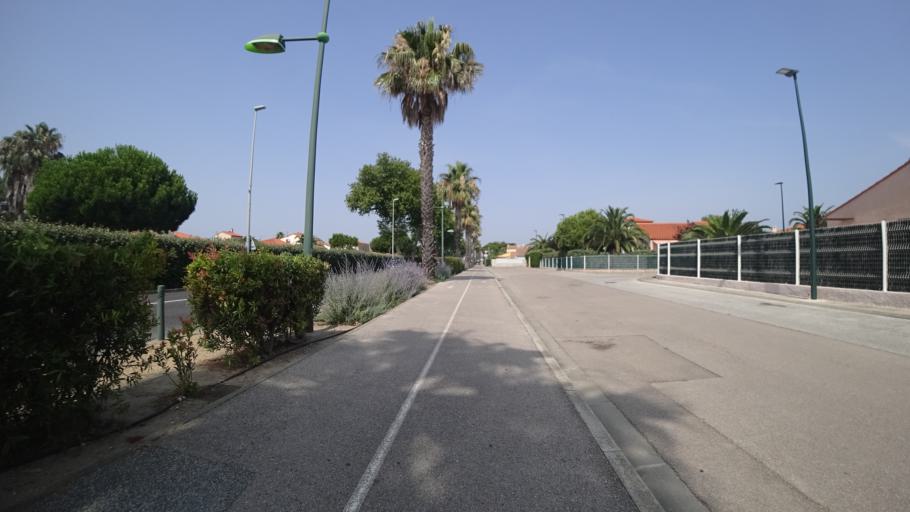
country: FR
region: Languedoc-Roussillon
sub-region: Departement des Pyrenees-Orientales
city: Saint-Laurent-de-la-Salanque
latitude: 42.7720
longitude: 3.0050
